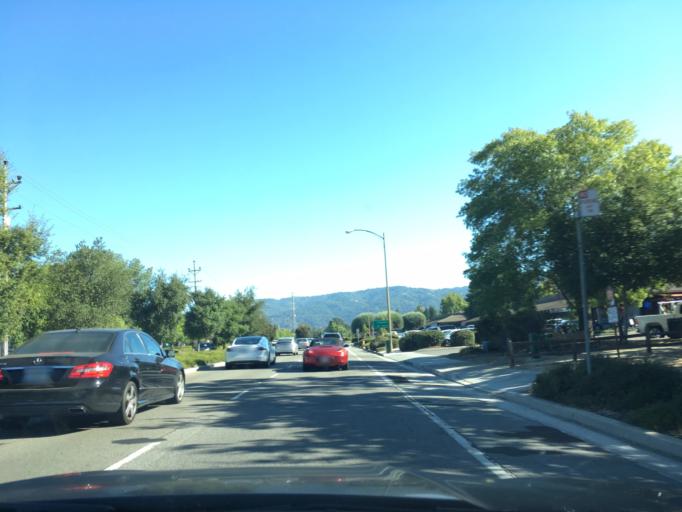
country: US
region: California
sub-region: Santa Clara County
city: Cupertino
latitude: 37.2927
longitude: -122.0324
